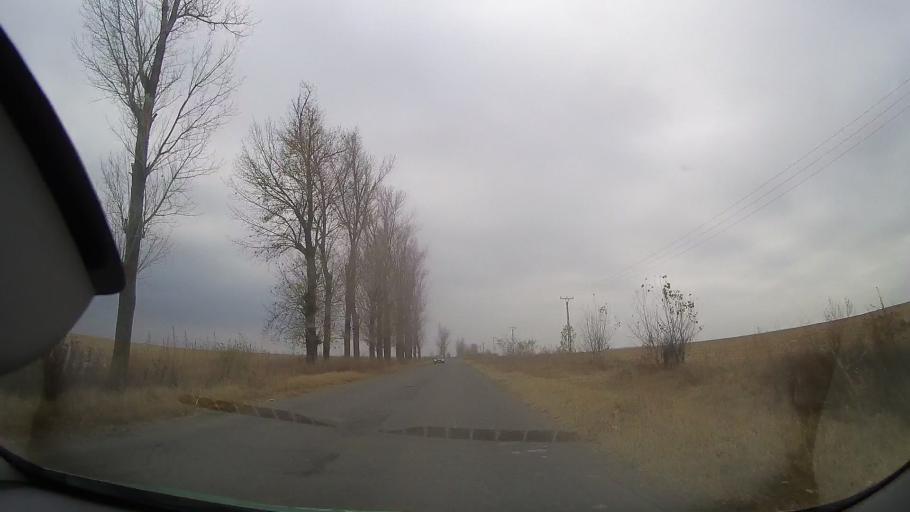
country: RO
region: Buzau
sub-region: Comuna Scutelnici
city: Scutelnici
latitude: 44.8837
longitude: 26.9534
